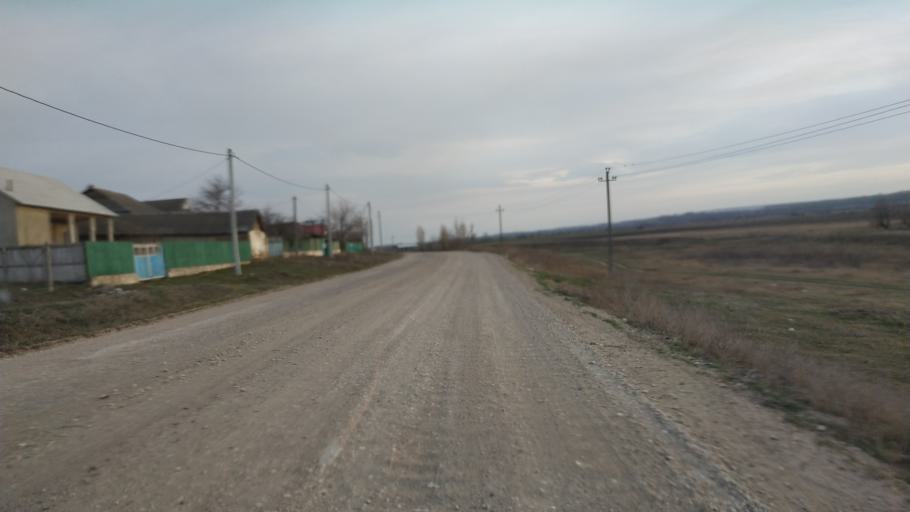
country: MD
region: Hincesti
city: Dancu
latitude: 46.7768
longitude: 28.1968
